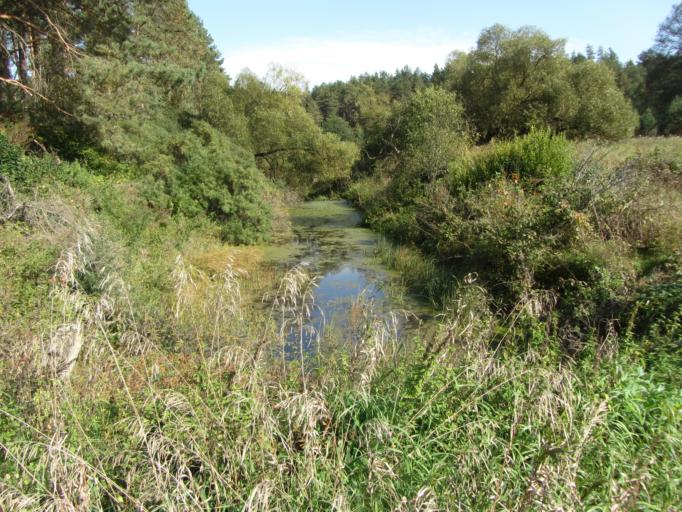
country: LT
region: Alytaus apskritis
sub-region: Alytaus rajonas
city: Daugai
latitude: 54.1015
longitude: 24.2771
